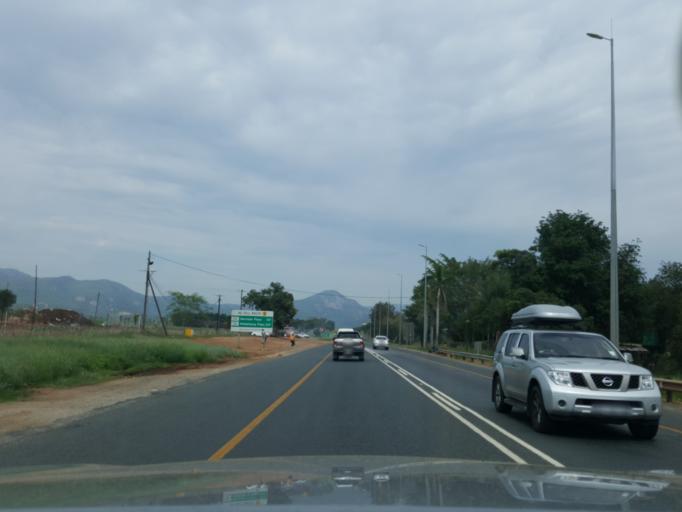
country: SZ
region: Hhohho
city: Ntfonjeni
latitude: -25.5365
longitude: 31.3420
